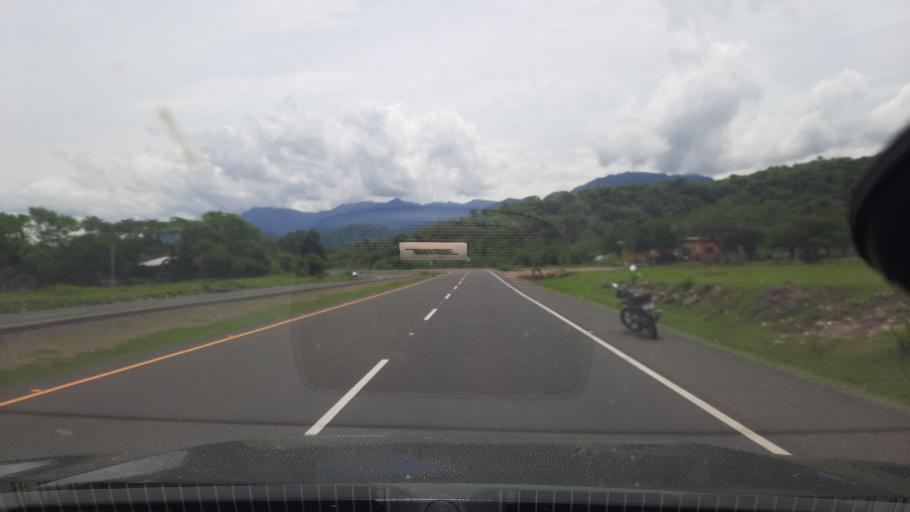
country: HN
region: Valle
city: Aramecina
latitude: 13.7079
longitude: -87.7090
